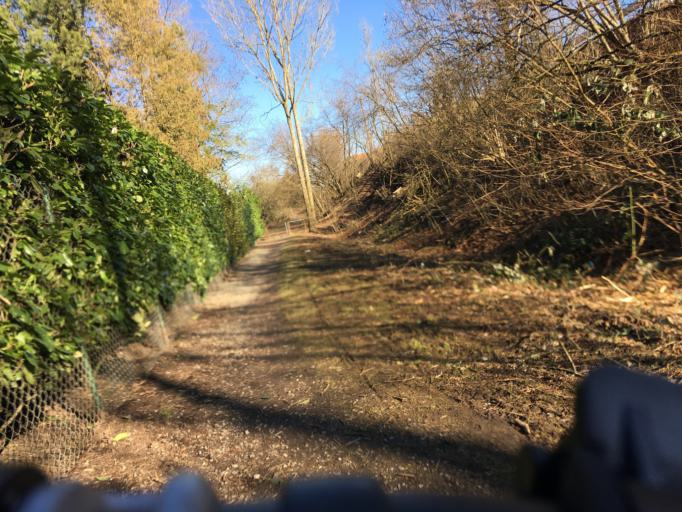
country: DE
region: Baden-Wuerttemberg
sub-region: Freiburg Region
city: Gottmadingen
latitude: 47.7379
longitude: 8.7798
